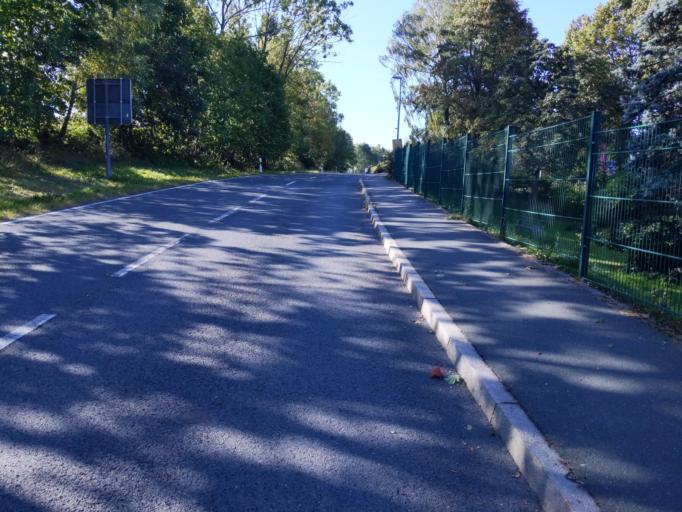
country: DE
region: Saxony
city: Pohl
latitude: 50.3981
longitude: 12.3440
